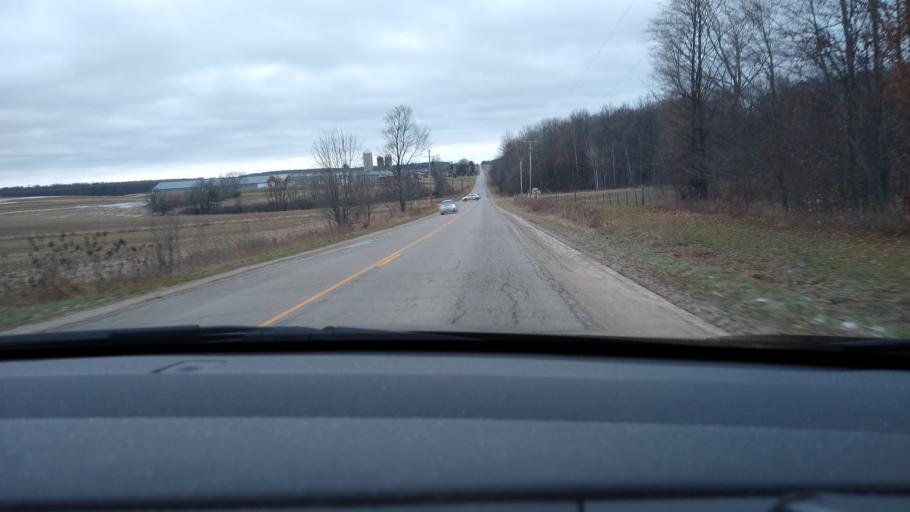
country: US
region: Michigan
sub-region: Missaukee County
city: Lake City
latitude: 44.2920
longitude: -85.0542
